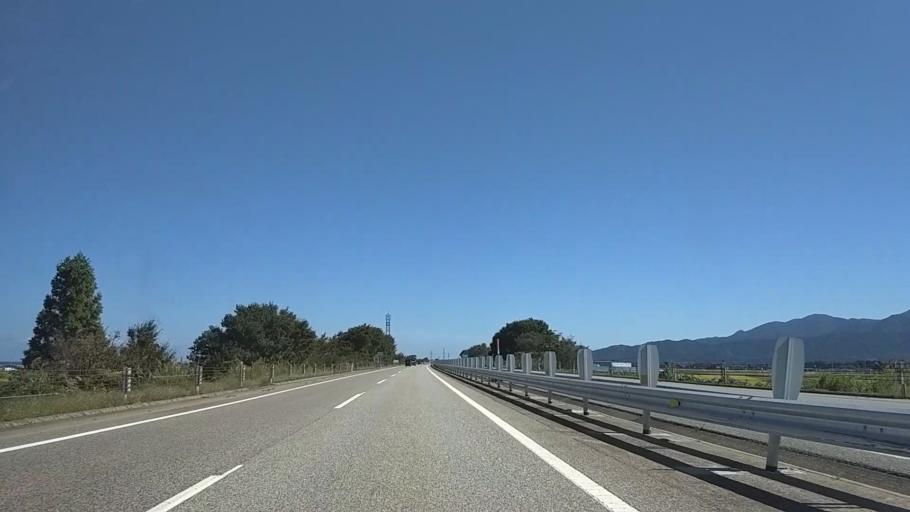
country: JP
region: Toyama
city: Nyuzen
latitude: 36.9090
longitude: 137.5057
